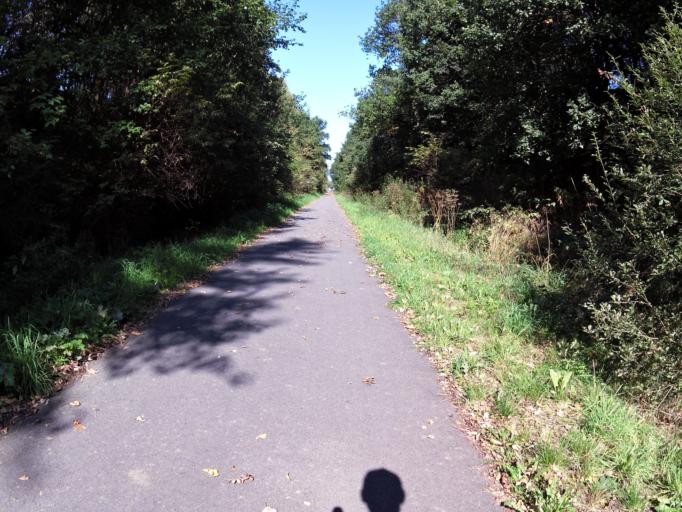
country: BE
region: Wallonia
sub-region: Province de Liege
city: Waimes
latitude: 50.4524
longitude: 6.1494
